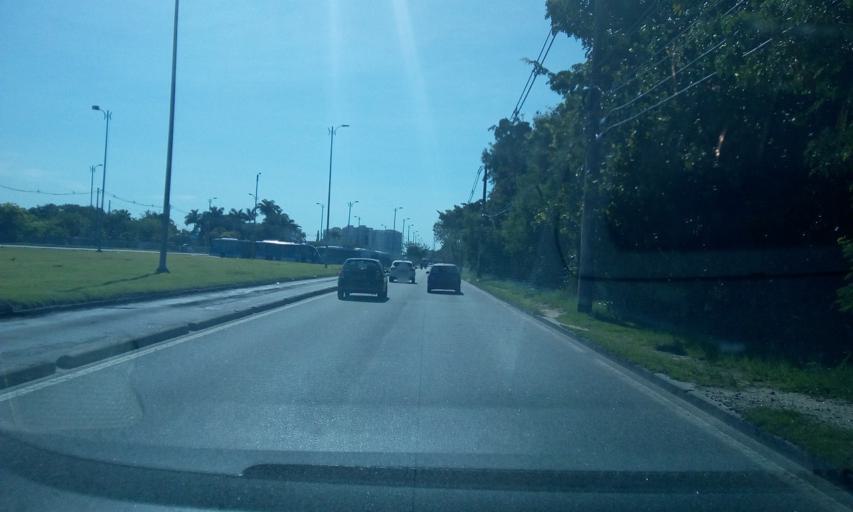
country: BR
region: Rio de Janeiro
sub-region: Nilopolis
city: Nilopolis
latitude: -23.0189
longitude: -43.5071
